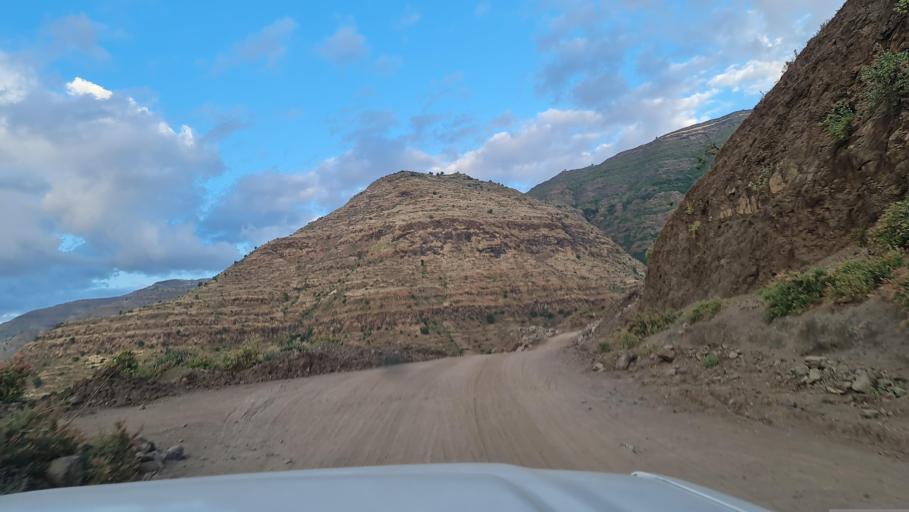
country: ET
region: Amhara
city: Debark'
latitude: 13.0148
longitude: 38.0512
